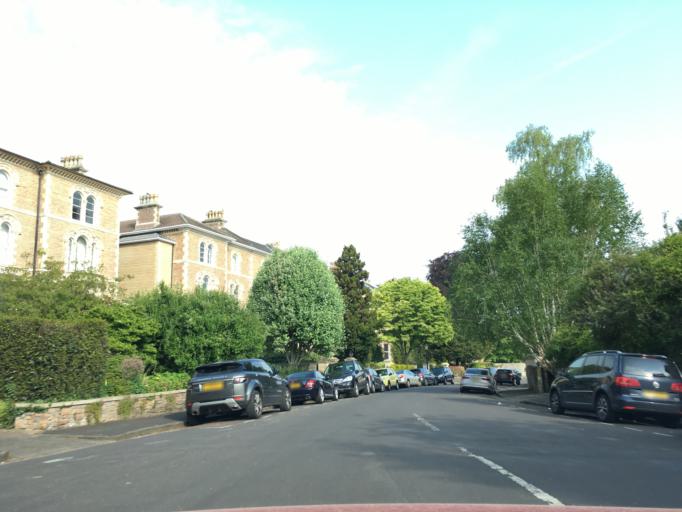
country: GB
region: England
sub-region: Bristol
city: Bristol
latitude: 51.4596
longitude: -2.6239
